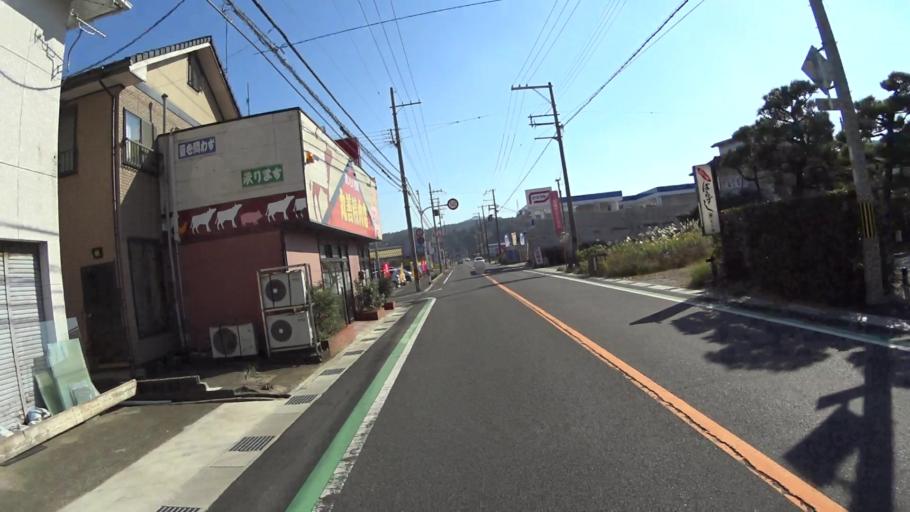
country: JP
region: Kyoto
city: Miyazu
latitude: 35.6732
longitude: 135.0280
